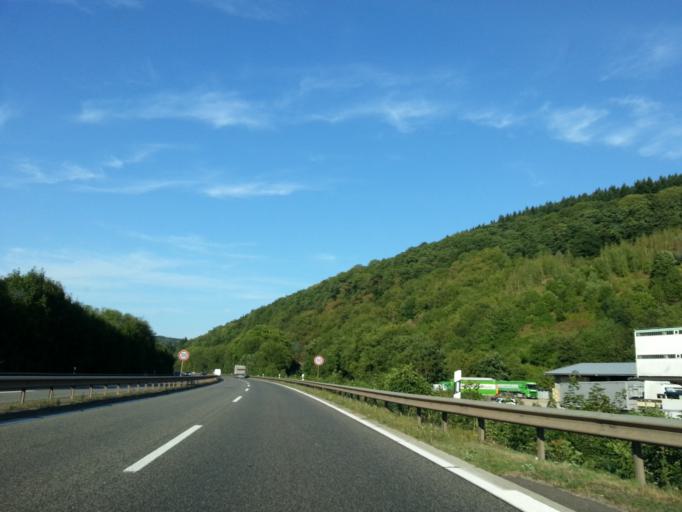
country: DE
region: Rheinland-Pfalz
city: Kenn
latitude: 49.7778
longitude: 6.6958
